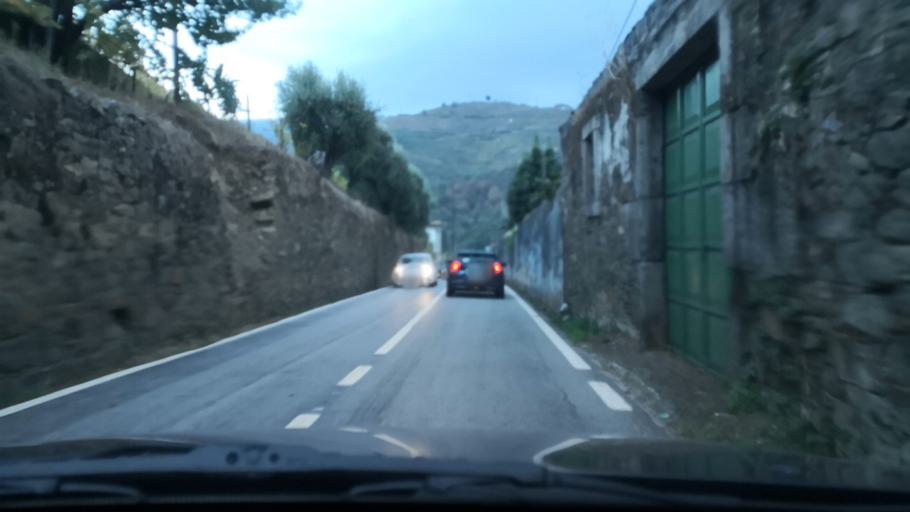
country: PT
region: Vila Real
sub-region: Mesao Frio
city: Mesao Frio
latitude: 41.1617
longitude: -7.8585
